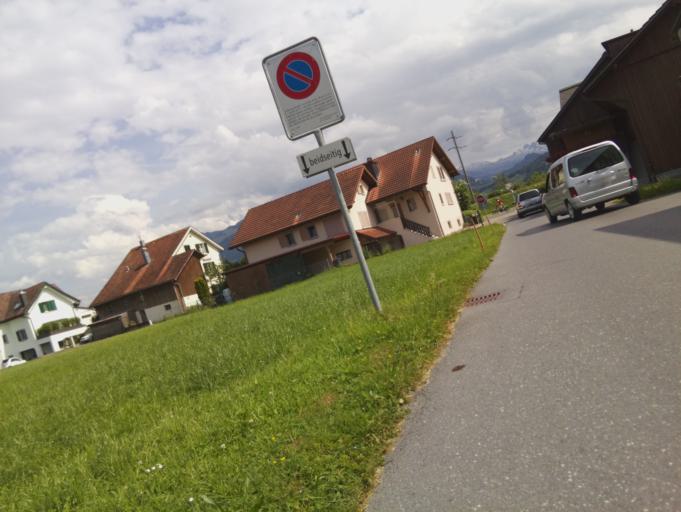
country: CH
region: Schwyz
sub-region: Bezirk March
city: Lachen
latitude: 47.1928
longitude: 8.8727
